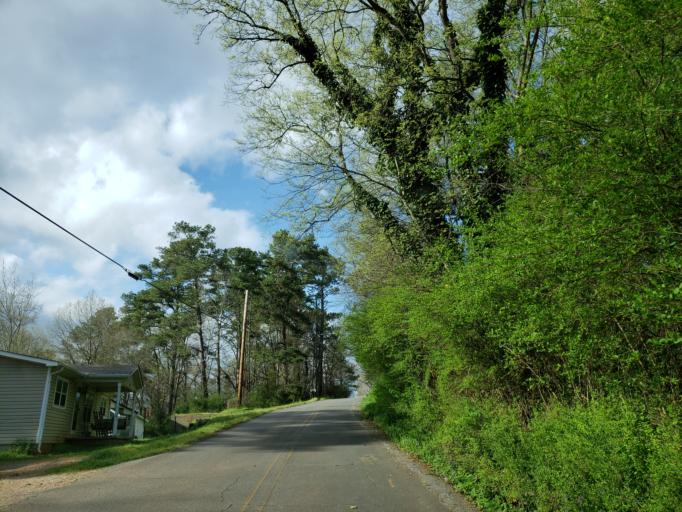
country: US
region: Georgia
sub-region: Bartow County
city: Emerson
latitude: 34.1287
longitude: -84.7596
